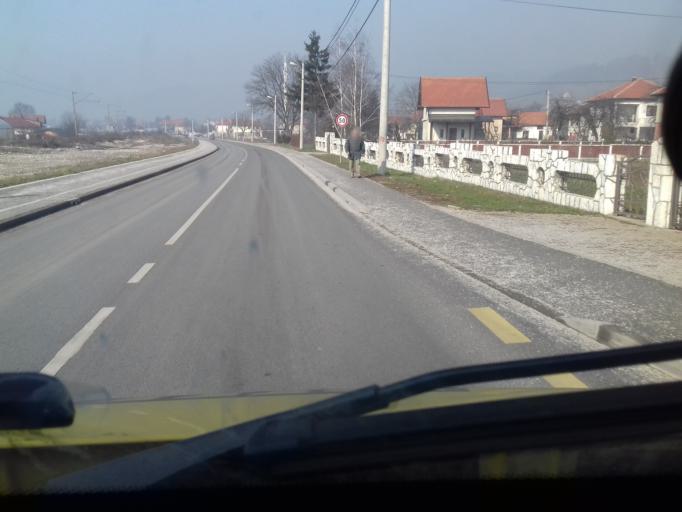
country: BA
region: Federation of Bosnia and Herzegovina
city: Mahala
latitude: 43.9836
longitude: 18.2387
